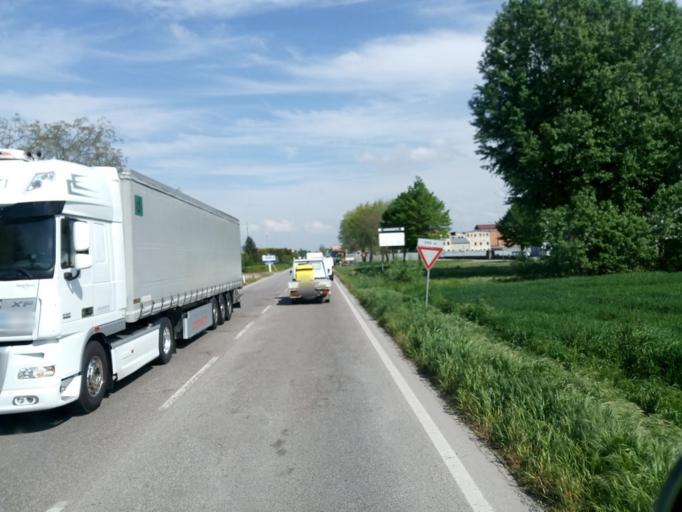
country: IT
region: Veneto
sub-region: Provincia di Verona
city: Sanguinetto
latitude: 45.1837
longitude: 11.1394
